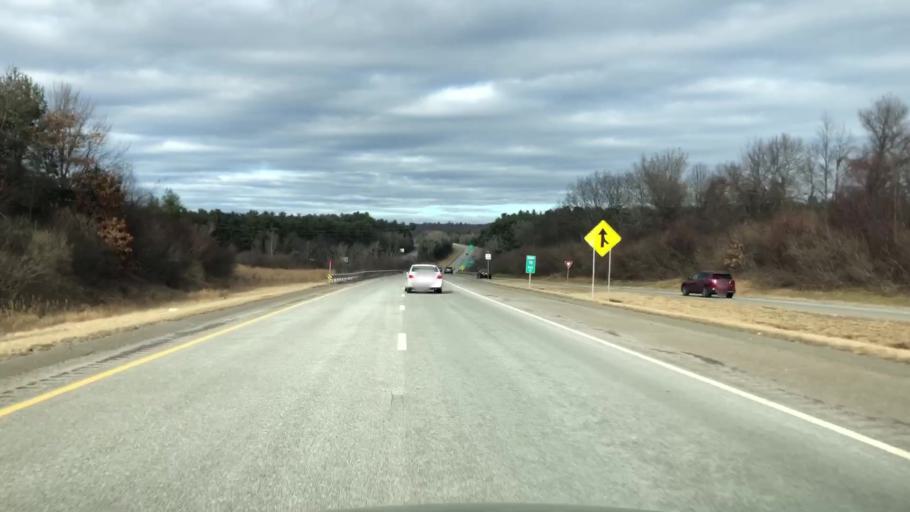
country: US
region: Massachusetts
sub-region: Worcester County
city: Leominster
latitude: 42.4930
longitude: -71.7231
